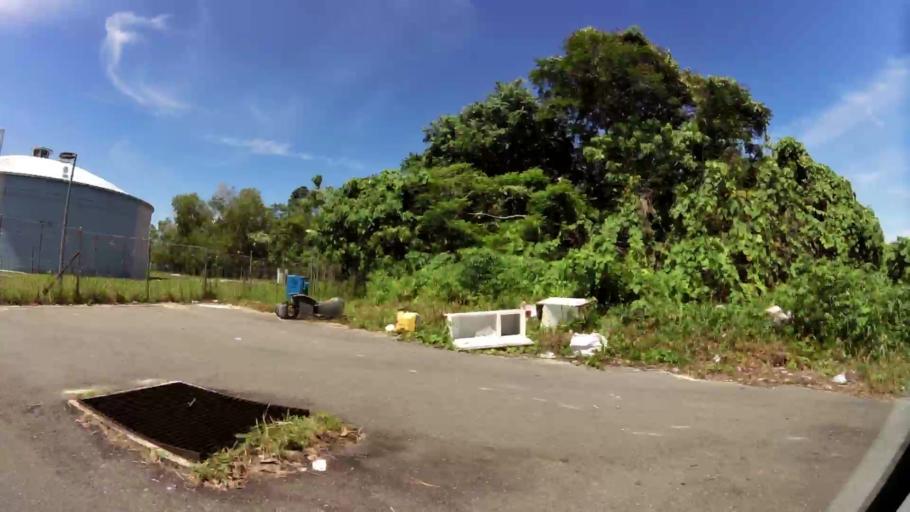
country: BN
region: Brunei and Muara
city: Bandar Seri Begawan
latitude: 4.9315
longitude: 114.9544
